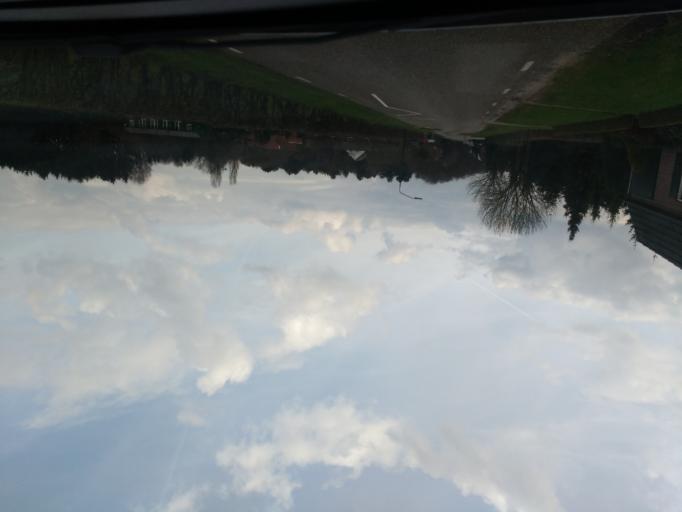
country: NL
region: Limburg
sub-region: Gemeente Venray
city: Venray
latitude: 51.5717
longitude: 6.0234
